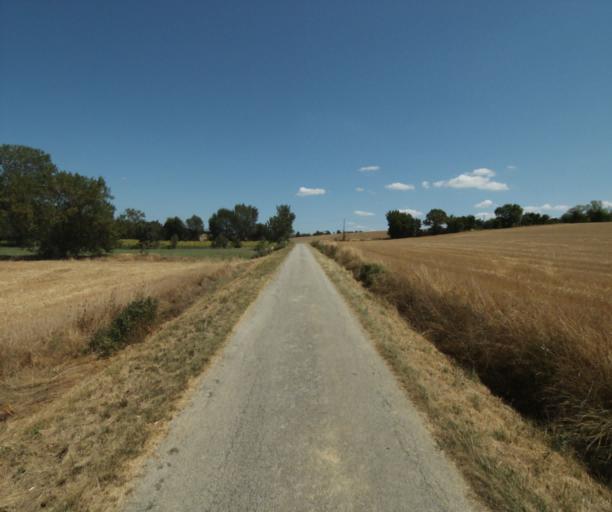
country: FR
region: Midi-Pyrenees
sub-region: Departement de la Haute-Garonne
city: Saint-Felix-Lauragais
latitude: 43.4826
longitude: 1.8957
